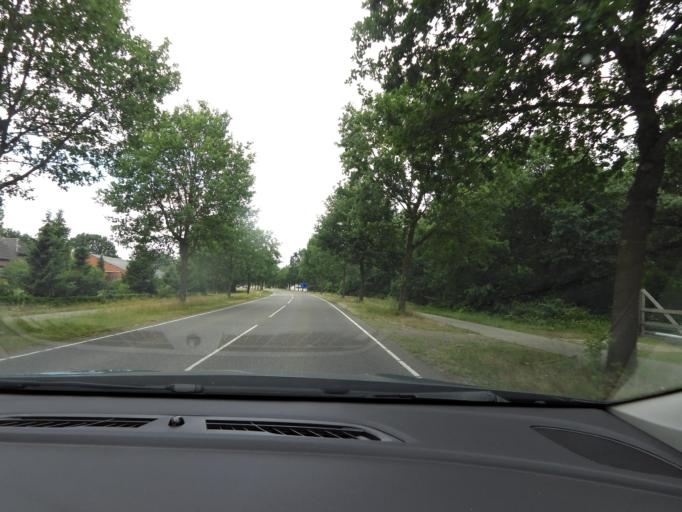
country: NL
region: North Brabant
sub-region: Gemeente Baarle-Nassau
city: Baarle-Nassau
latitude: 51.4556
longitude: 4.9152
